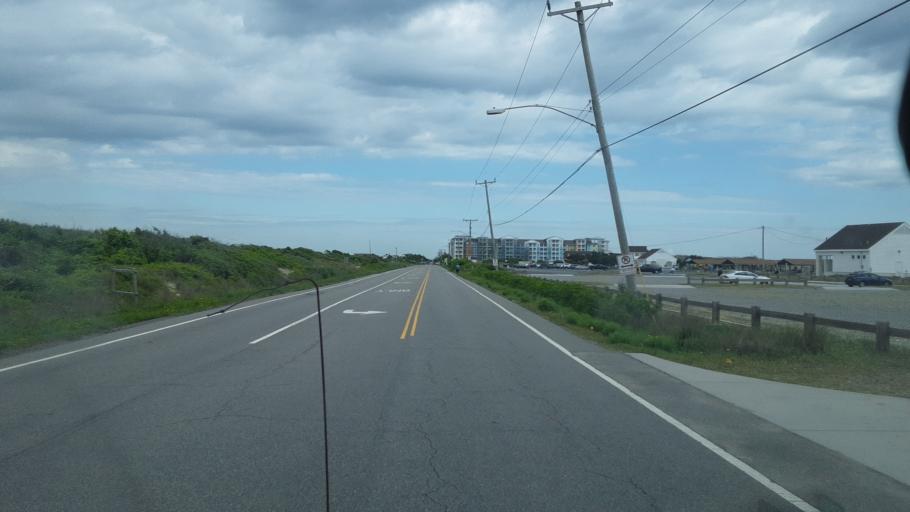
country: US
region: Virginia
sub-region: City of Virginia Beach
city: Virginia Beach
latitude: 36.6909
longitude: -75.9241
